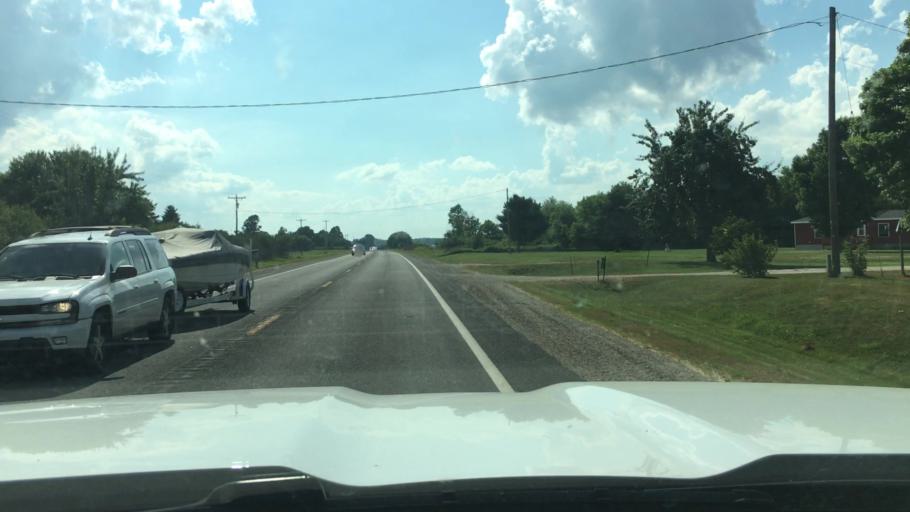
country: US
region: Michigan
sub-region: Montcalm County
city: Stanton
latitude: 43.1780
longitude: -85.0474
